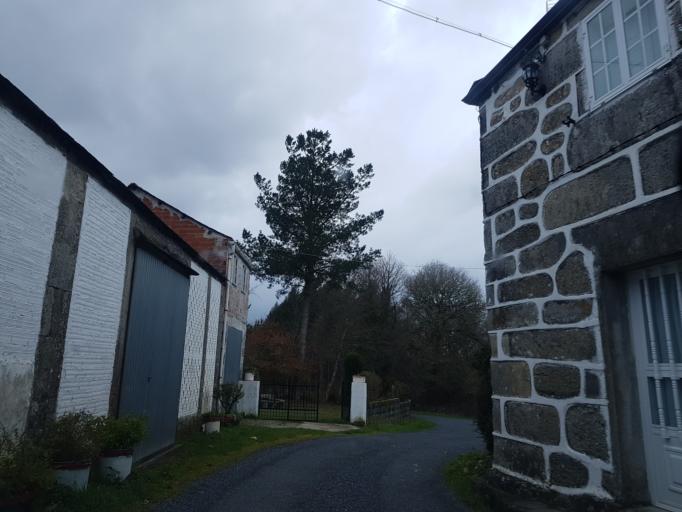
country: ES
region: Galicia
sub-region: Provincia de Lugo
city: Friol
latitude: 43.1216
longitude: -7.8172
